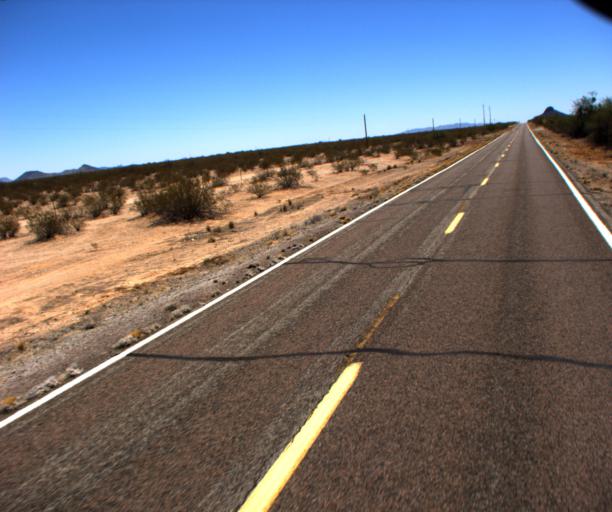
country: US
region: Arizona
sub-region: Pima County
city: Ajo
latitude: 32.2069
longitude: -112.5816
